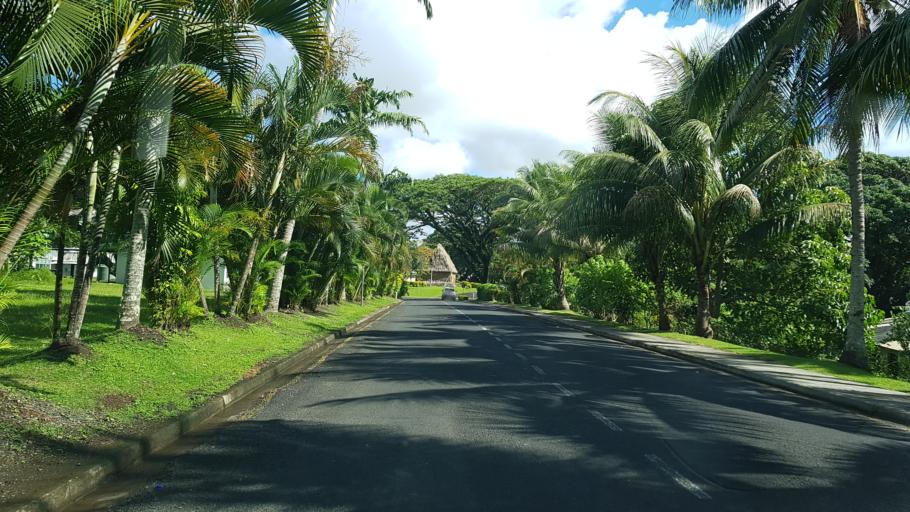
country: FJ
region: Central
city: Suva
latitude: -18.1528
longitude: 178.4437
